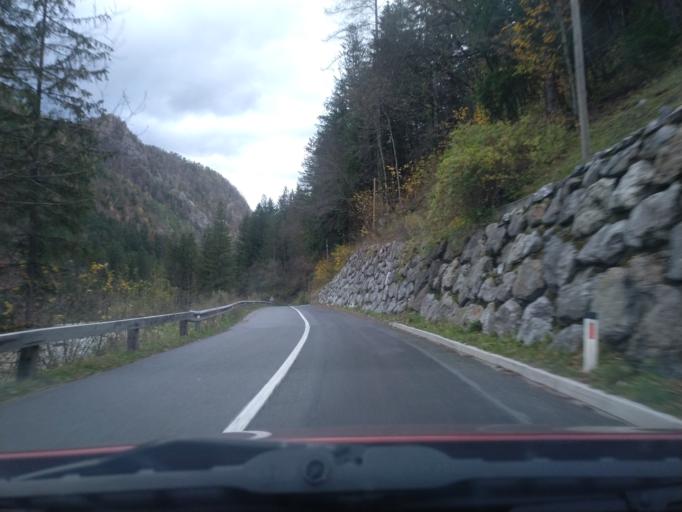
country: SI
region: Luce
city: Luce
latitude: 46.3749
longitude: 14.7349
